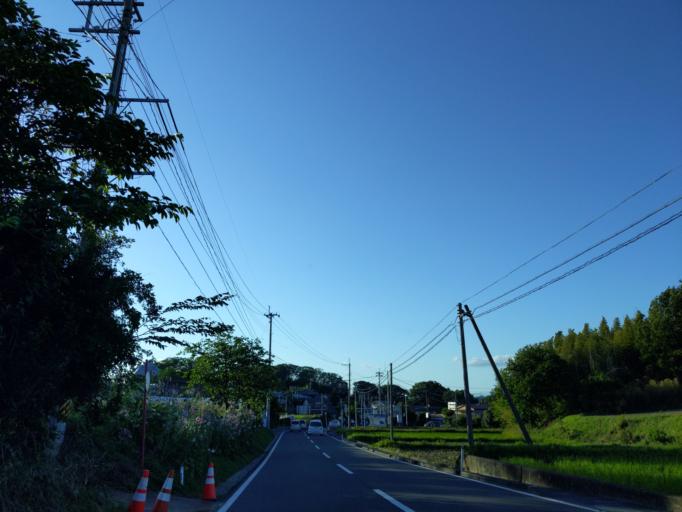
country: JP
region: Fukushima
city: Koriyama
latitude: 37.4052
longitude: 140.4130
